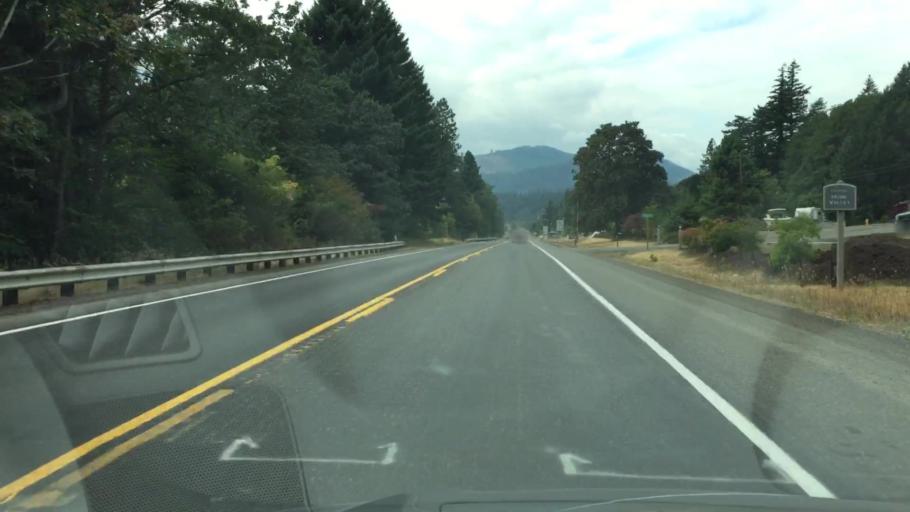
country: US
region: Washington
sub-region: Skamania County
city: Carson
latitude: 45.7090
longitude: -121.7703
